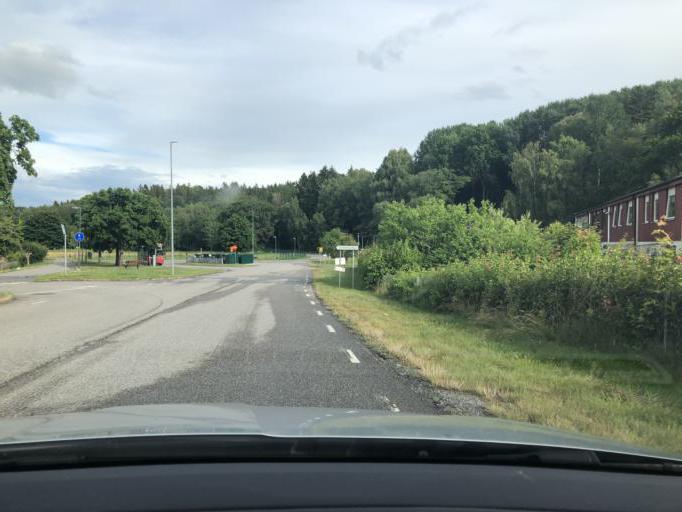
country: SE
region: Stockholm
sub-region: Botkyrka Kommun
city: Alby
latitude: 59.2328
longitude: 17.8632
